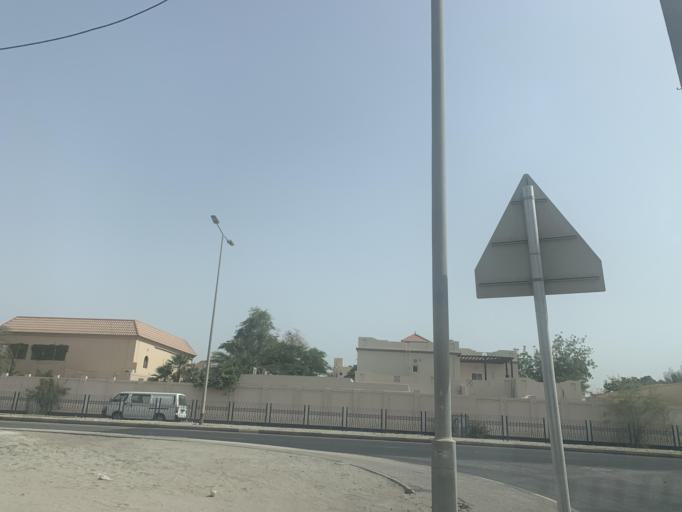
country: BH
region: Manama
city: Jidd Hafs
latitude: 26.2205
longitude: 50.5436
